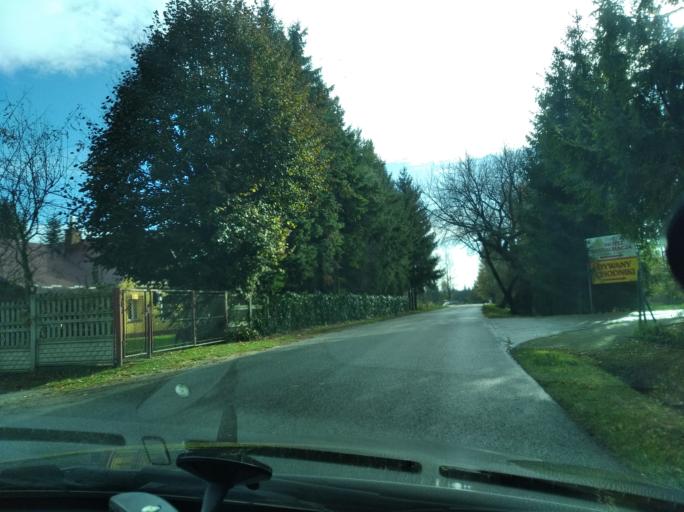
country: PL
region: Subcarpathian Voivodeship
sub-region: Powiat ropczycko-sedziszowski
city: Ostrow
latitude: 50.0916
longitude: 21.5645
